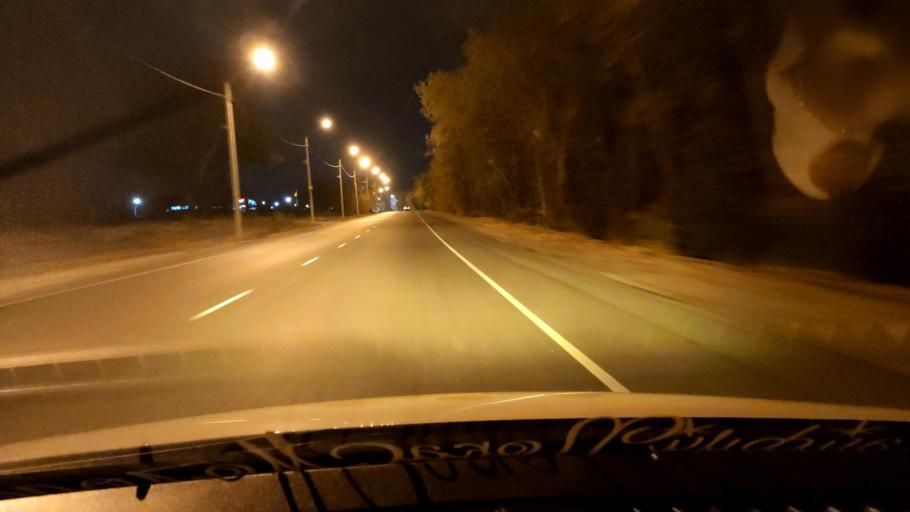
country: RU
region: Voronezj
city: Voronezh
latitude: 51.6123
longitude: 39.1792
